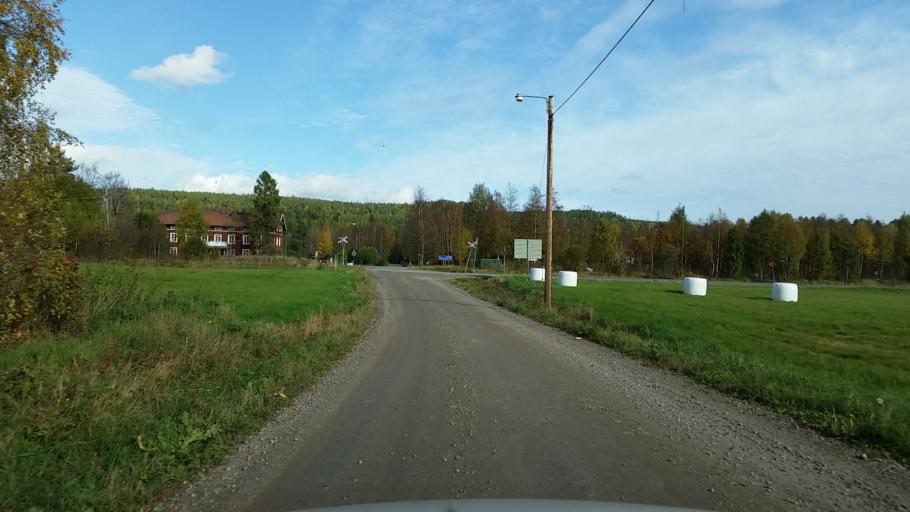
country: SE
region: Gaevleborg
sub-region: Ljusdals Kommun
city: Jaervsoe
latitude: 61.7930
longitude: 16.2041
